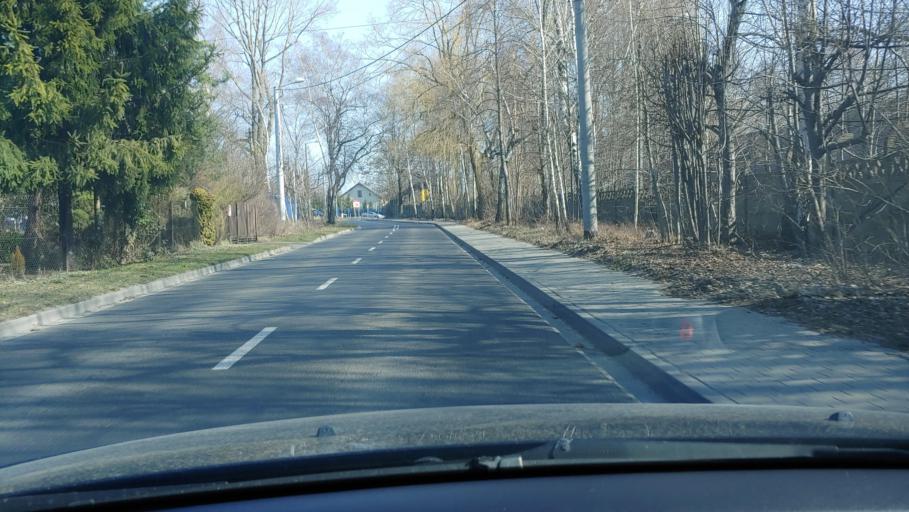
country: PL
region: Lesser Poland Voivodeship
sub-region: Powiat chrzanowski
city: Trzebinia
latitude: 50.1592
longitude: 19.4532
